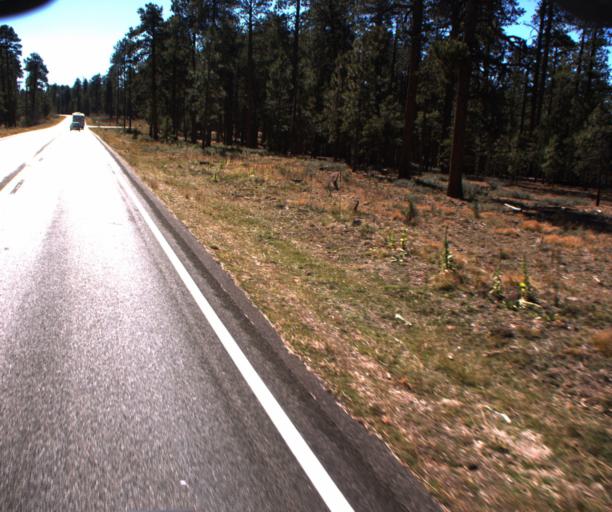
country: US
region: Arizona
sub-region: Coconino County
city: Fredonia
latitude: 36.6617
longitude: -112.1904
